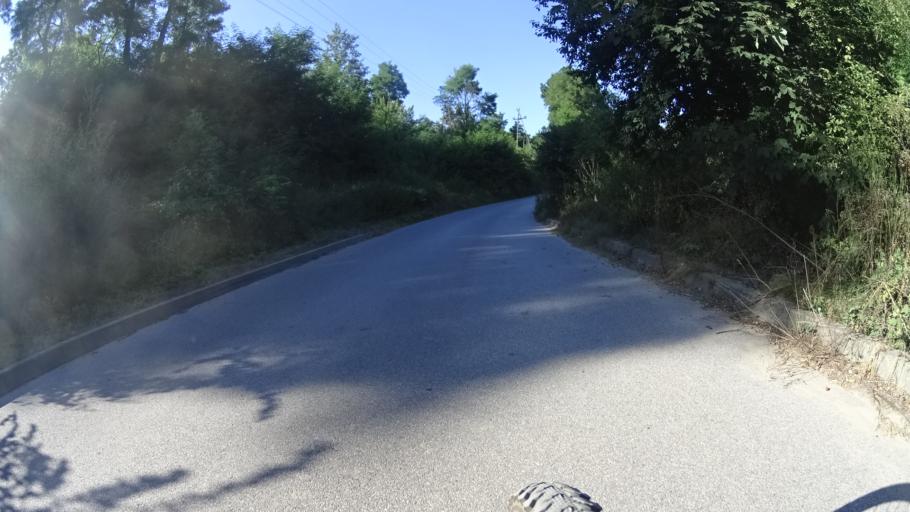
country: PL
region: Masovian Voivodeship
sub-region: Powiat bialobrzeski
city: Bialobrzegi
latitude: 51.6673
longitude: 20.8882
